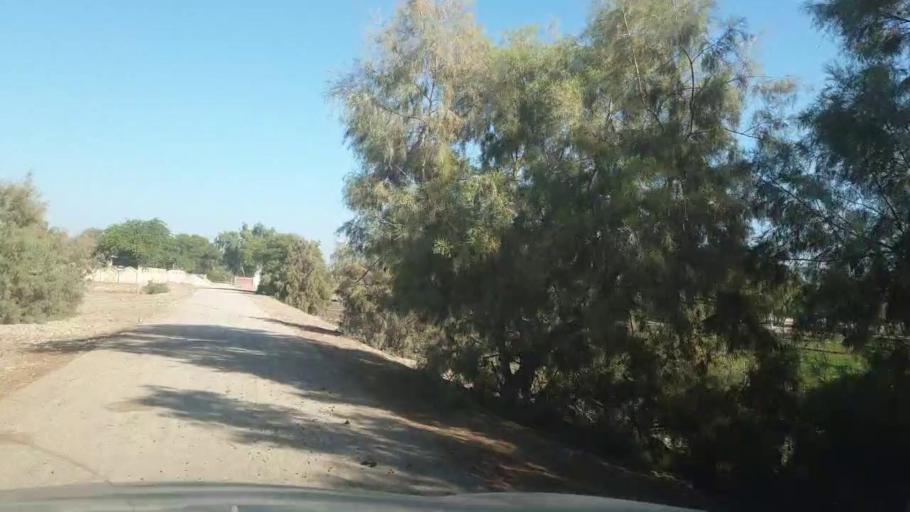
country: PK
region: Sindh
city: Bhan
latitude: 26.5416
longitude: 67.6592
